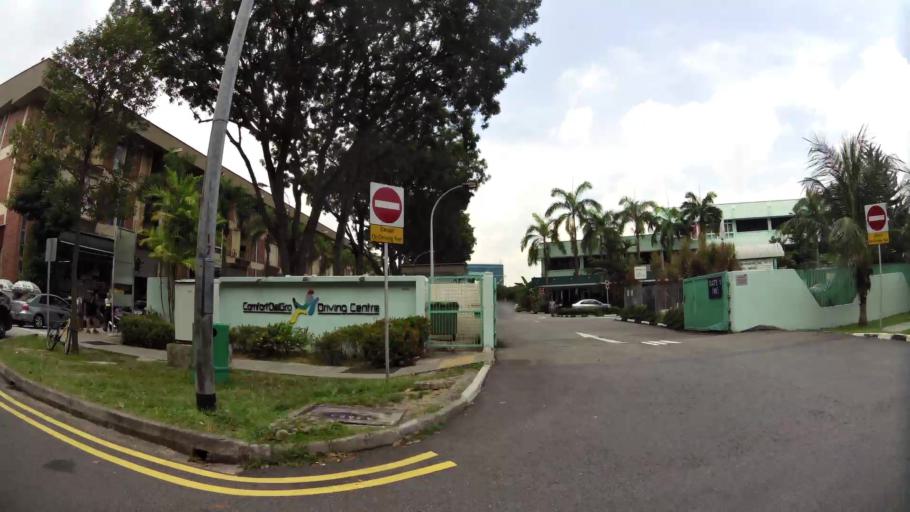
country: SG
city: Singapore
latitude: 1.3352
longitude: 103.8966
